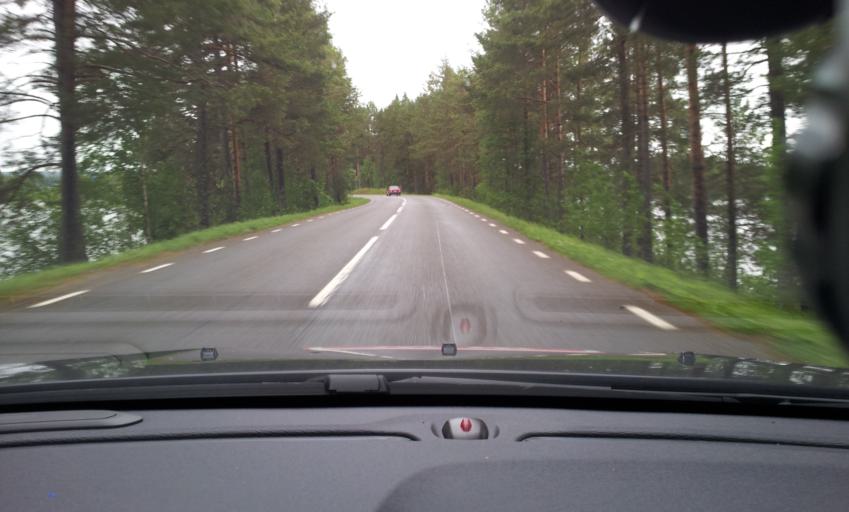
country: SE
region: Jaemtland
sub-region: Stroemsunds Kommun
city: Stroemsund
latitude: 63.5097
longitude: 15.4596
